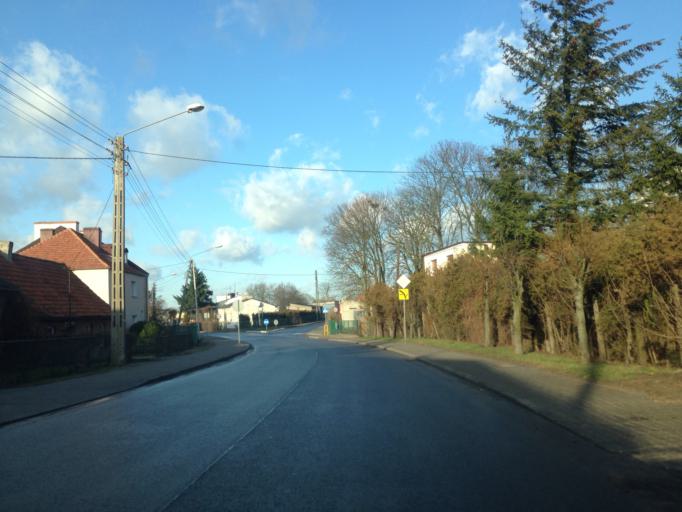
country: PL
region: Kujawsko-Pomorskie
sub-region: Powiat grudziadzki
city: Lasin
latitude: 53.5221
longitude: 19.0863
